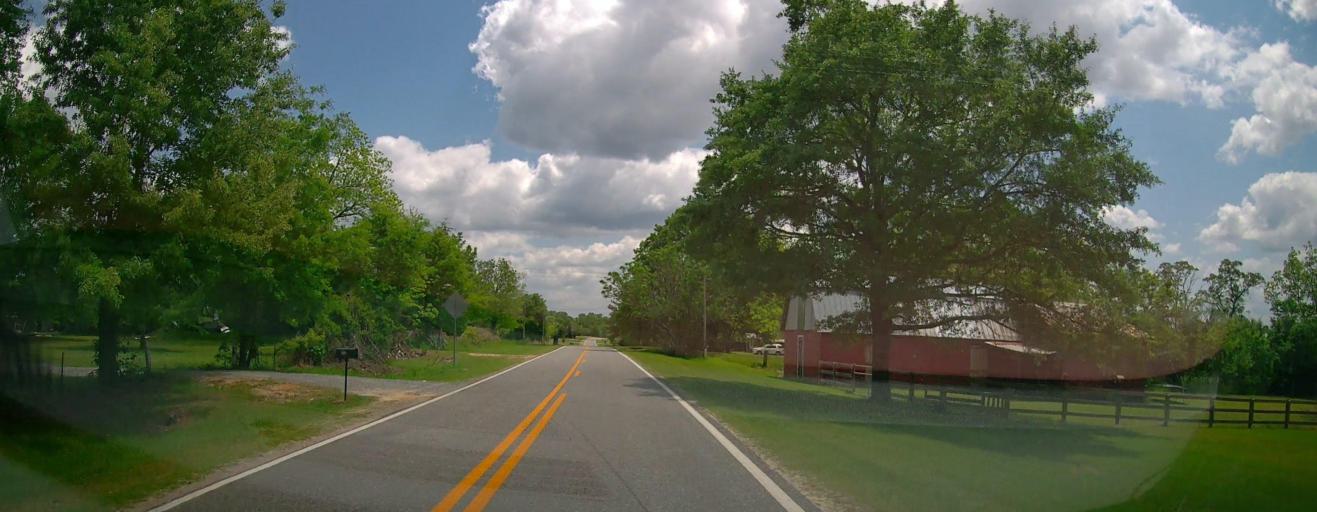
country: US
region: Georgia
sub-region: Laurens County
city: East Dublin
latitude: 32.5596
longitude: -82.8201
